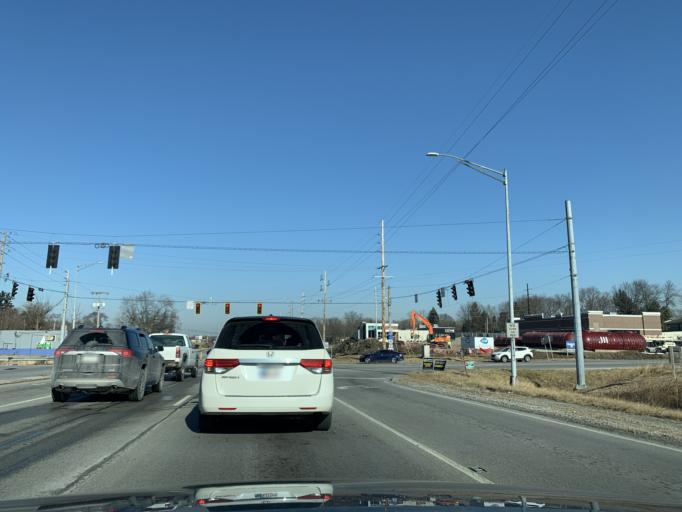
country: US
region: Indiana
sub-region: Lake County
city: Saint John
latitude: 41.4208
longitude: -87.4700
